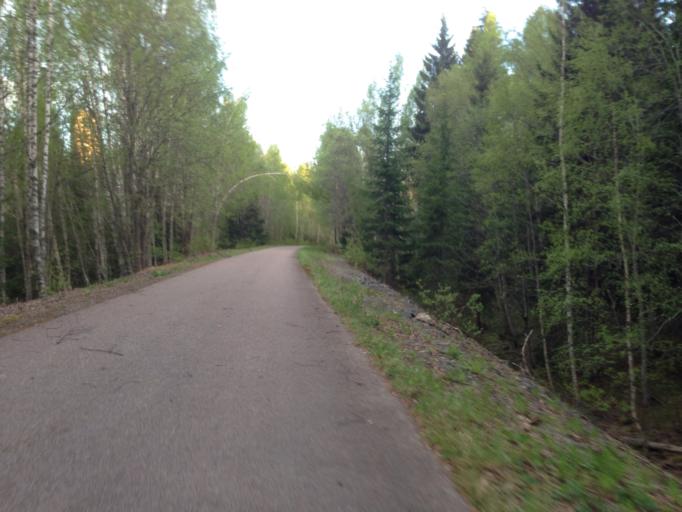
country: SE
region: Dalarna
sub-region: Ludvika Kommun
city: Grangesberg
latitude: 60.1274
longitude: 15.0701
